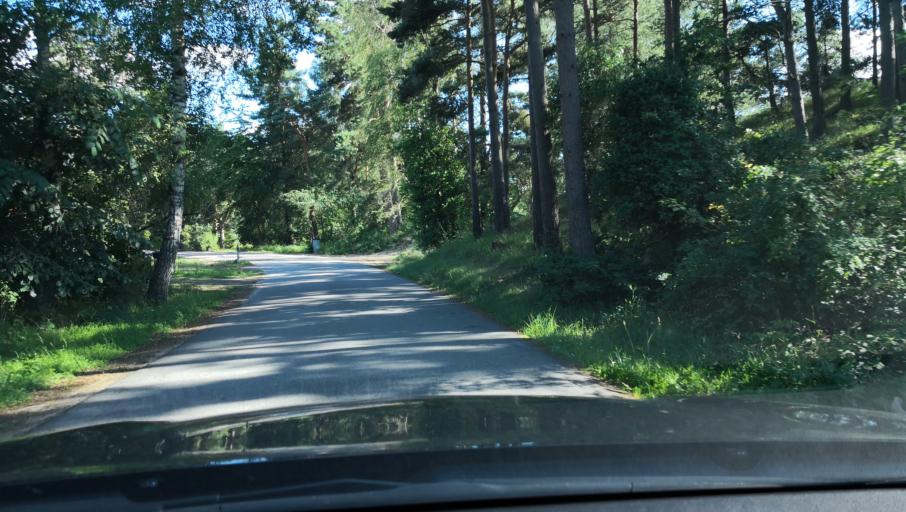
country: SE
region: Skane
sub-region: Simrishamns Kommun
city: Kivik
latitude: 55.7774
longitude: 14.1948
